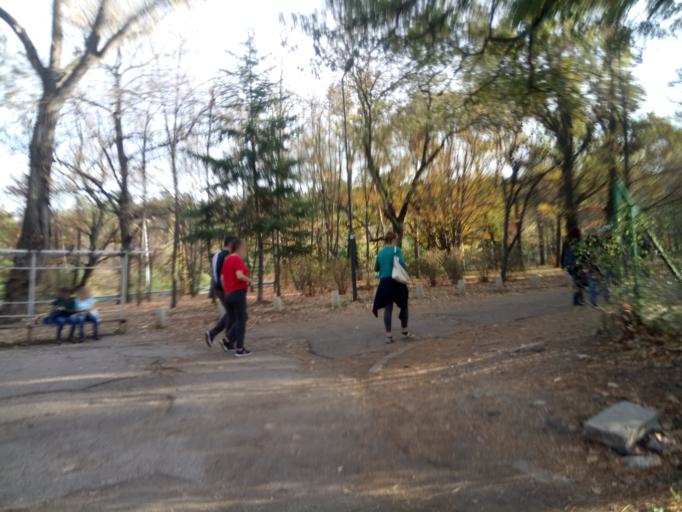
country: BG
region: Sofia-Capital
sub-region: Stolichna Obshtina
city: Sofia
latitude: 42.6818
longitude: 23.3452
